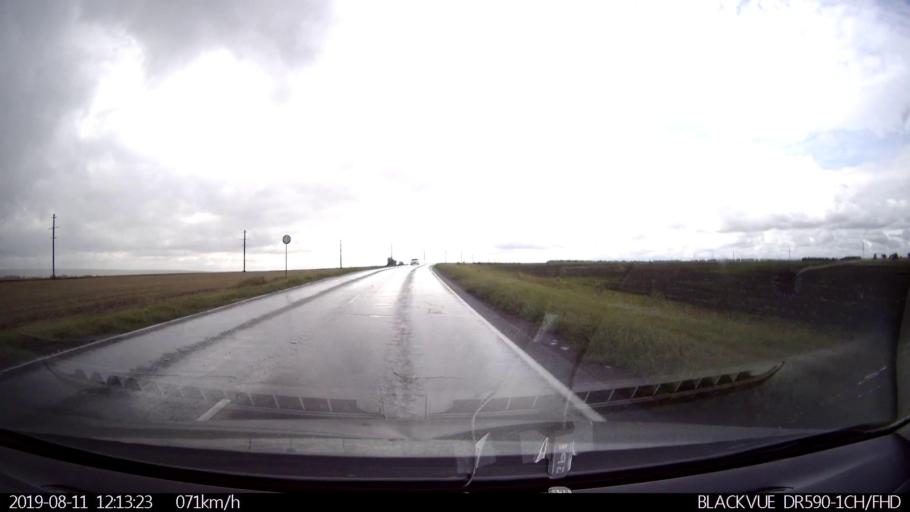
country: RU
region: Ulyanovsk
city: Silikatnyy
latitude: 53.9624
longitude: 47.9924
